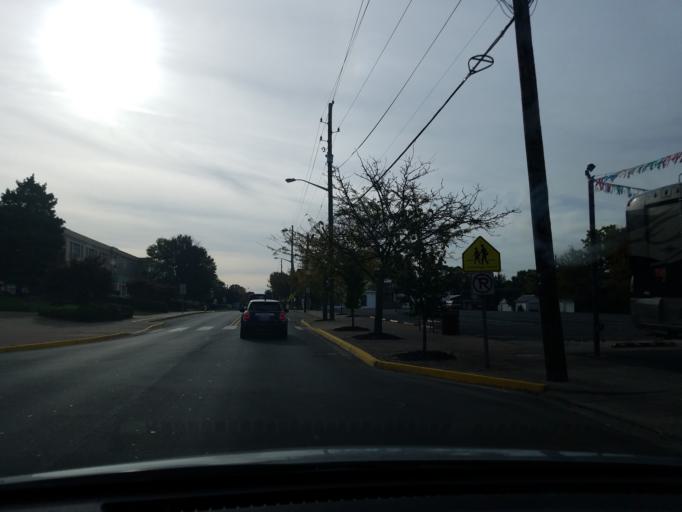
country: US
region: Indiana
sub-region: Floyd County
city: New Albany
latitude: 38.2990
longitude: -85.8127
